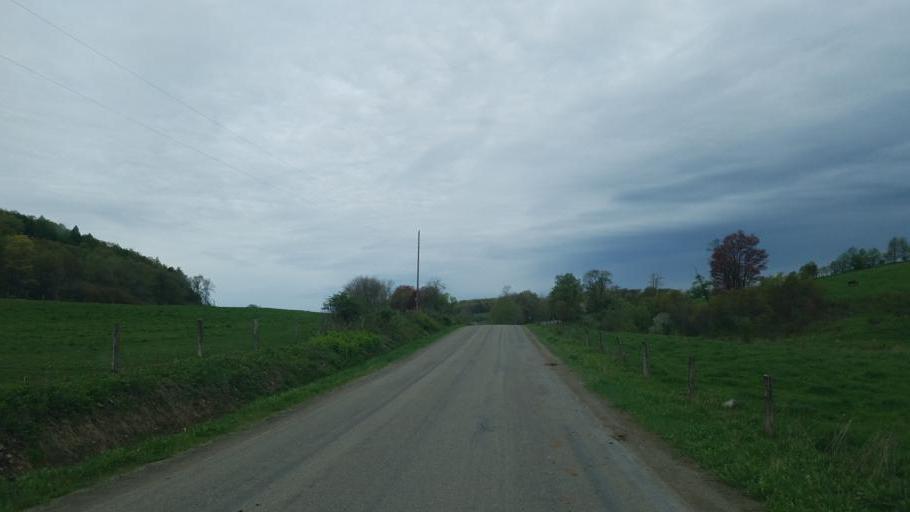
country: US
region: Pennsylvania
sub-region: Tioga County
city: Westfield
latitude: 41.9211
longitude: -77.7535
